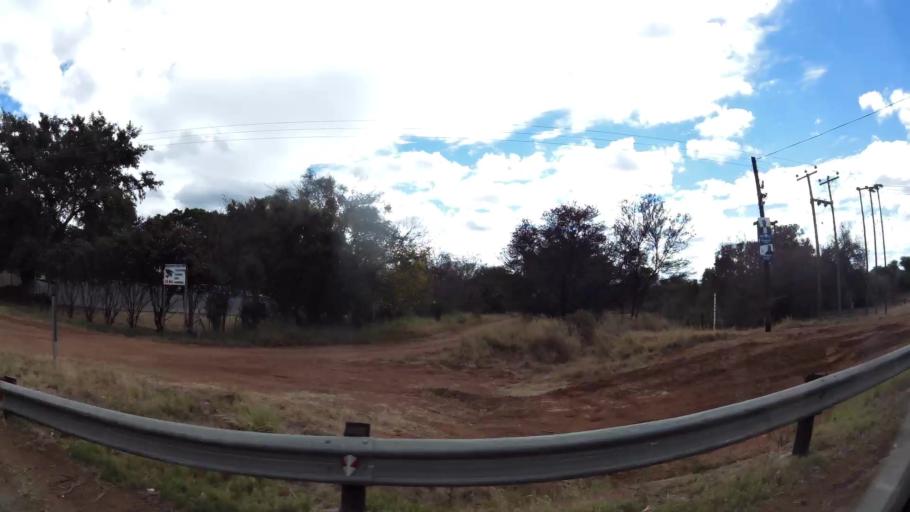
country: ZA
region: Limpopo
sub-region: Waterberg District Municipality
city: Warmbaths
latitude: -24.9018
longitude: 28.2778
